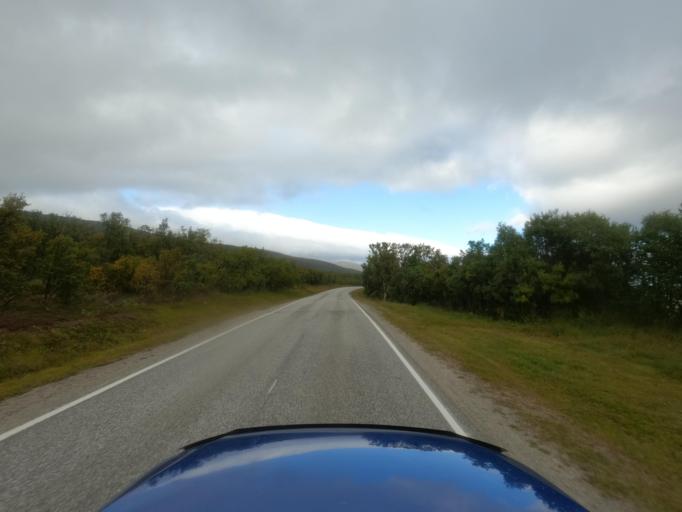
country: NO
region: Finnmark Fylke
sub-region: Porsanger
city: Lakselv
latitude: 70.4574
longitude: 25.2260
